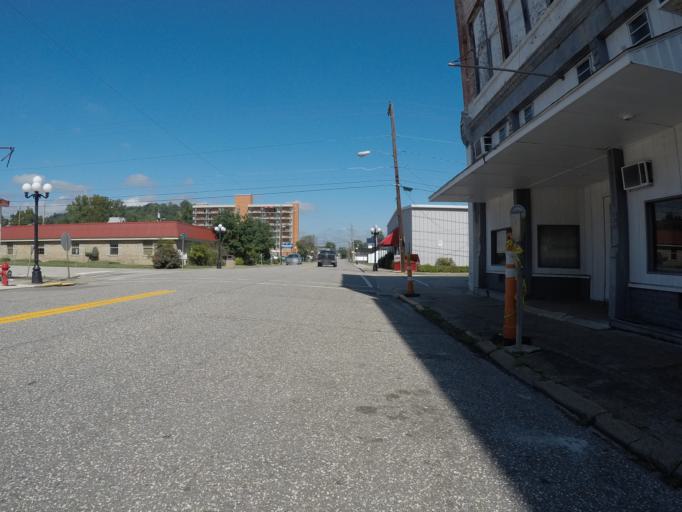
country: US
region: Ohio
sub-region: Lawrence County
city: South Point
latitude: 38.4180
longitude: -82.5976
